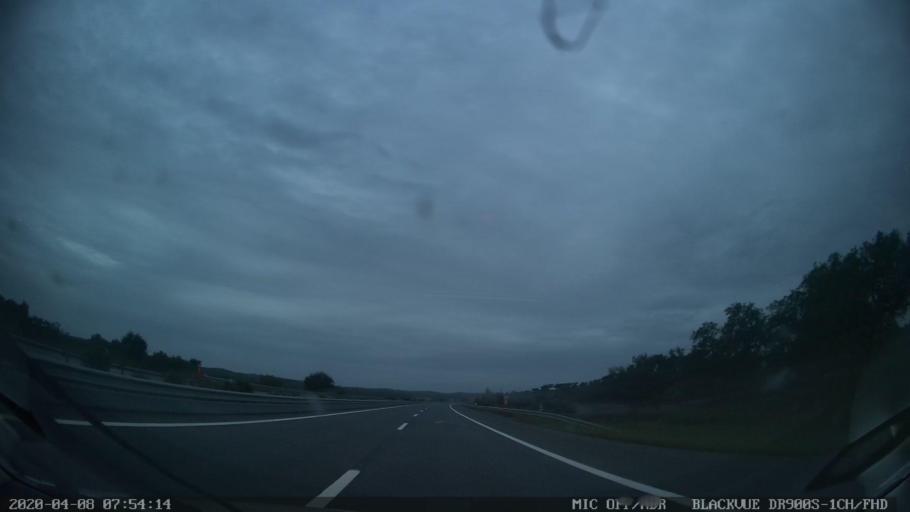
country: PT
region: Evora
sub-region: Estremoz
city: Estremoz
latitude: 38.7454
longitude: -7.7387
